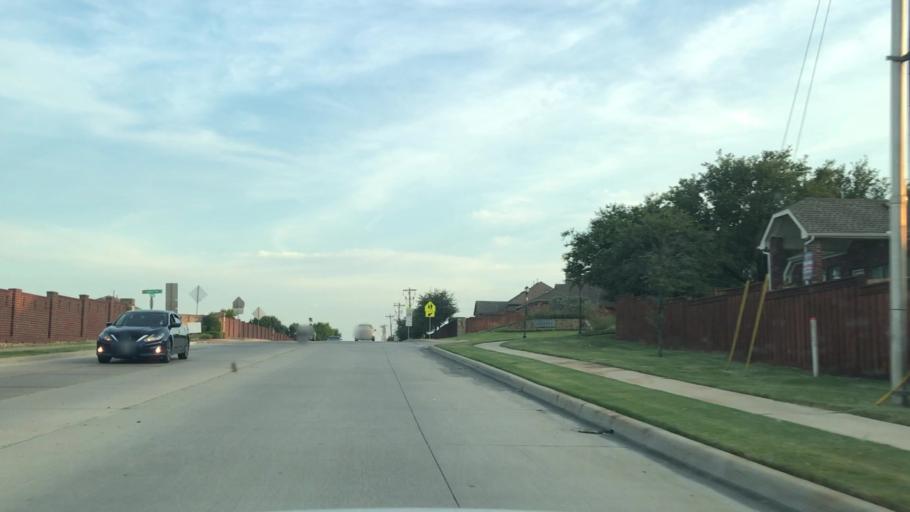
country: US
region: Texas
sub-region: Tarrant County
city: Keller
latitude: 32.9627
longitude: -97.2812
